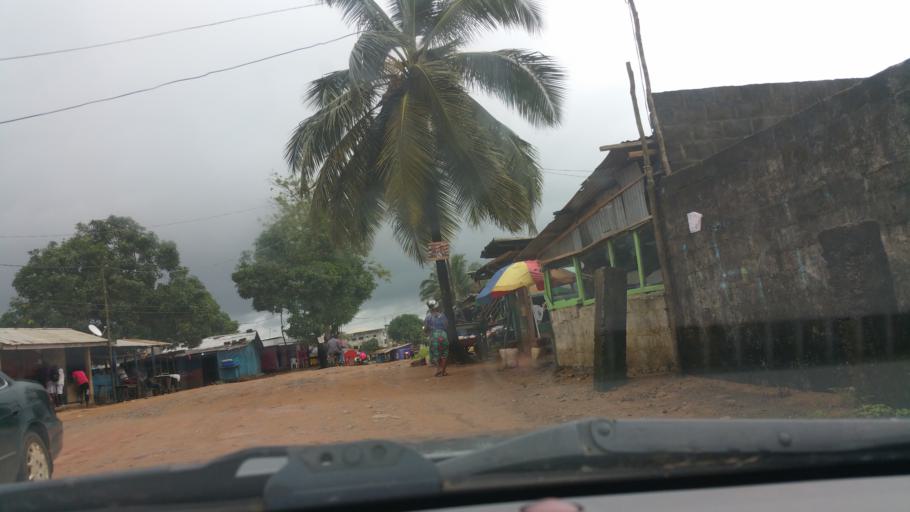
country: LR
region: Montserrado
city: Monrovia
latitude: 6.2338
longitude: -10.6693
